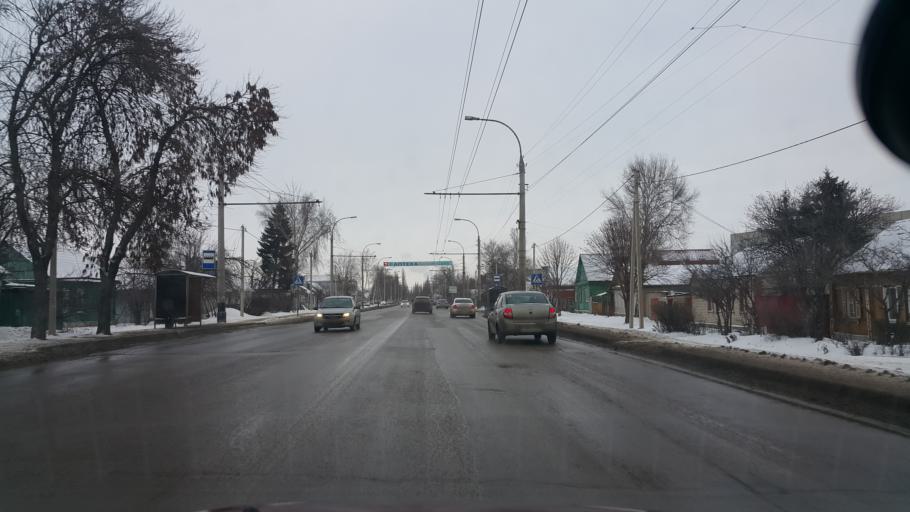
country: RU
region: Tambov
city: Tambov
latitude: 52.7293
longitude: 41.4026
